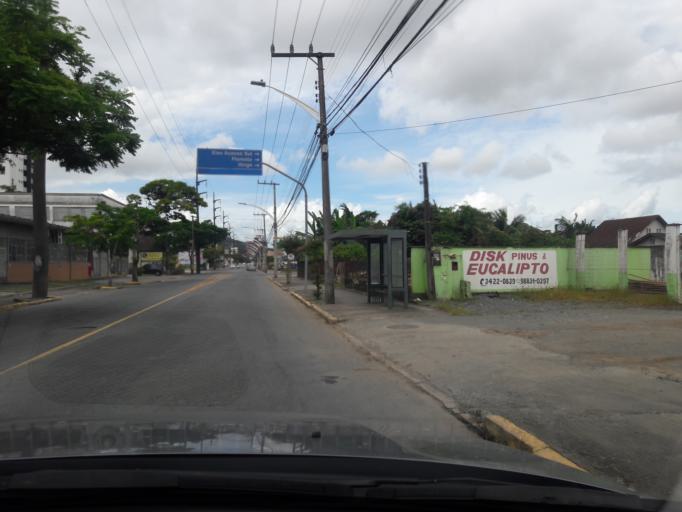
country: BR
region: Santa Catarina
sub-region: Joinville
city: Joinville
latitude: -26.3230
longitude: -48.8540
